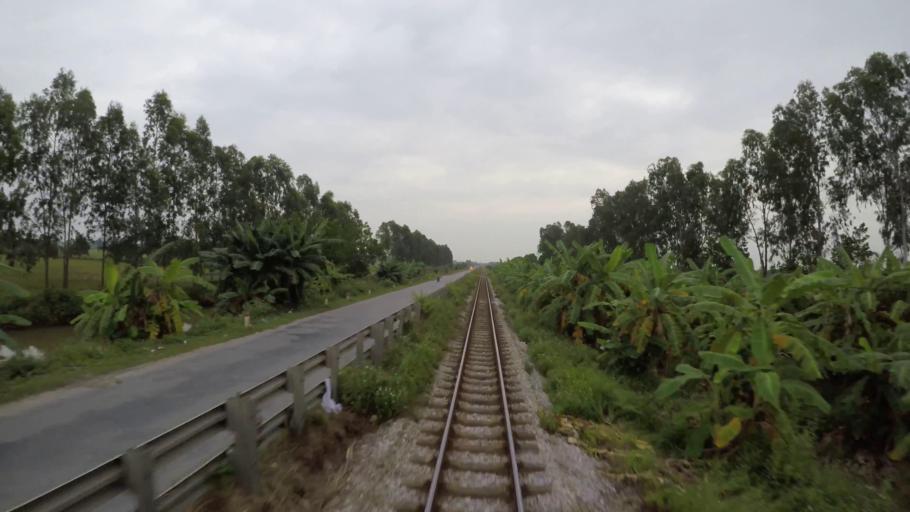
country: VN
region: Hung Yen
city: Ban Yen Nhan
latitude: 20.9852
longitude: 106.0671
